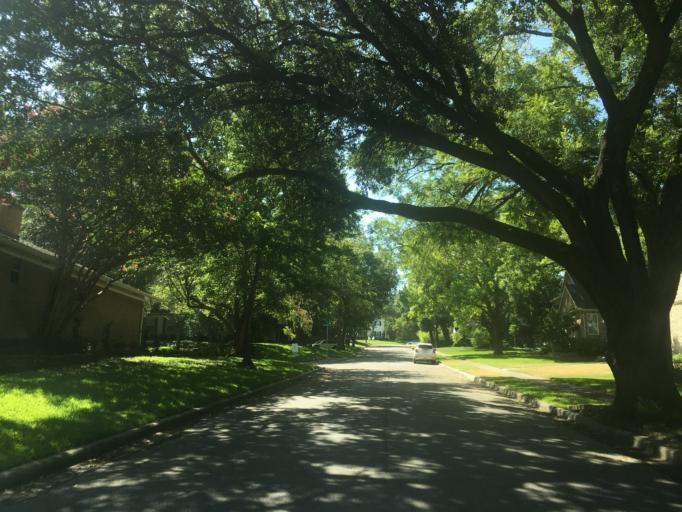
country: US
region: Texas
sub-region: Dallas County
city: Richardson
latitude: 32.8737
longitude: -96.7224
